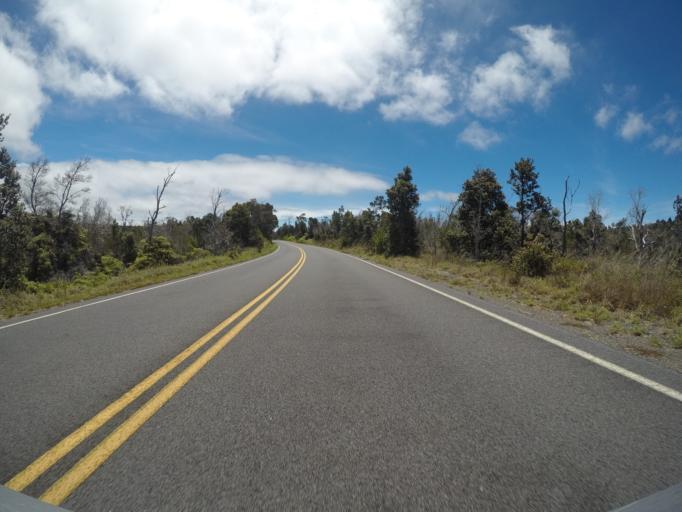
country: US
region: Hawaii
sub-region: Hawaii County
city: Volcano
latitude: 19.3718
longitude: -155.2327
